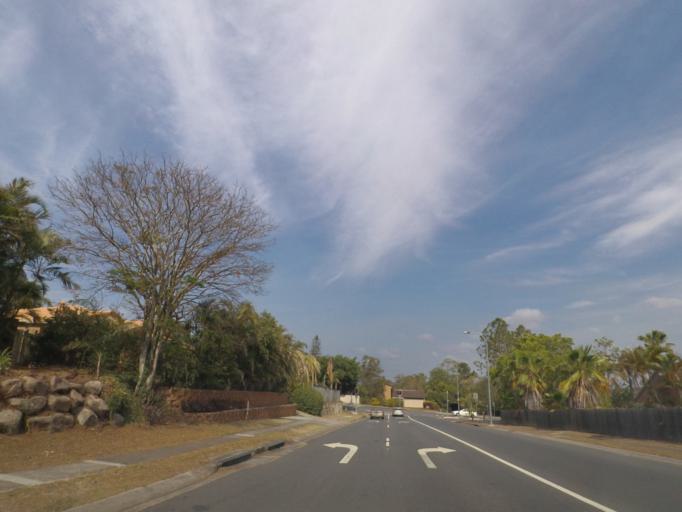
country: AU
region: Queensland
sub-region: Brisbane
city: Sunnybank Hills
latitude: -27.6001
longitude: 153.0632
